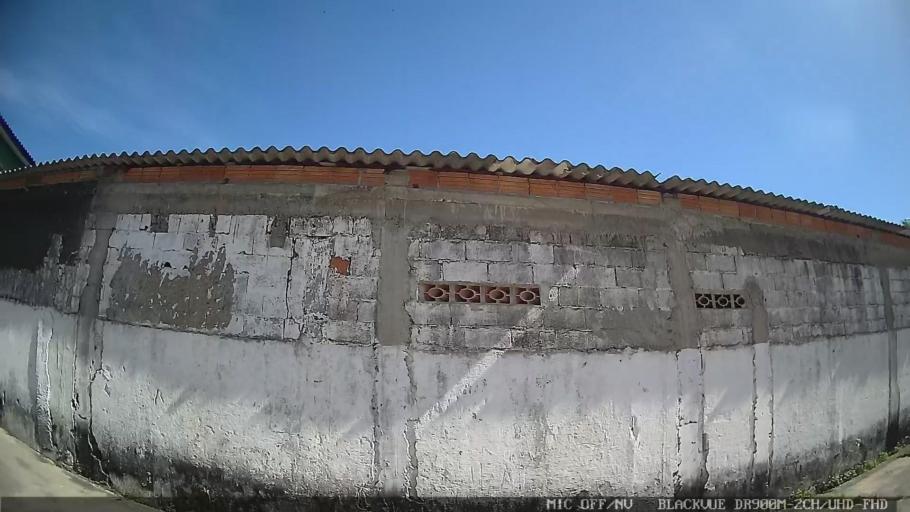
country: BR
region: Sao Paulo
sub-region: Guaruja
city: Guaruja
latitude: -23.9664
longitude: -46.2769
